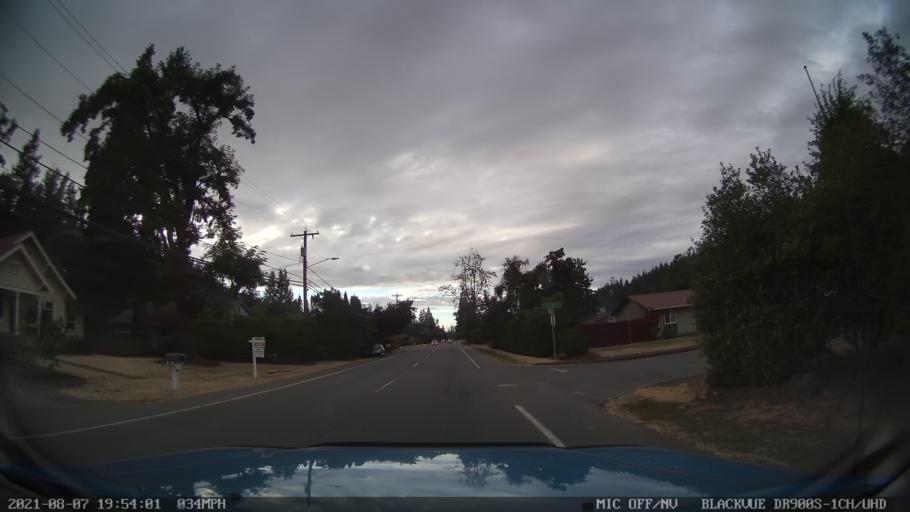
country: US
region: Oregon
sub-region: Marion County
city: Silverton
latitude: 44.9921
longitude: -122.7703
